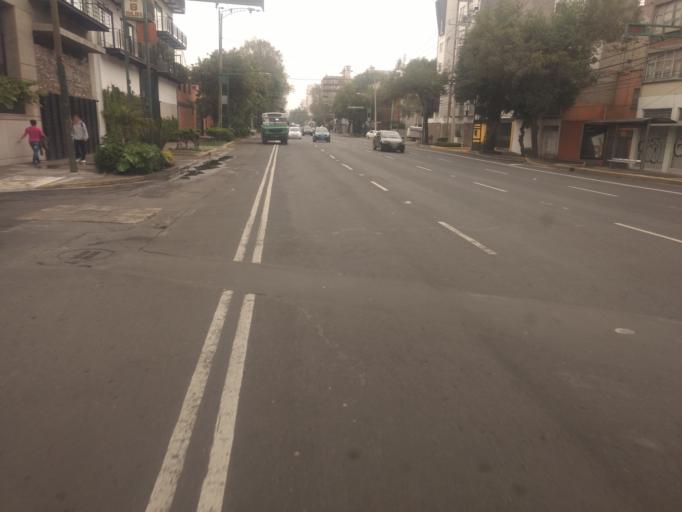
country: MX
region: Mexico City
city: Coyoacan
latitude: 19.3608
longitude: -99.1483
